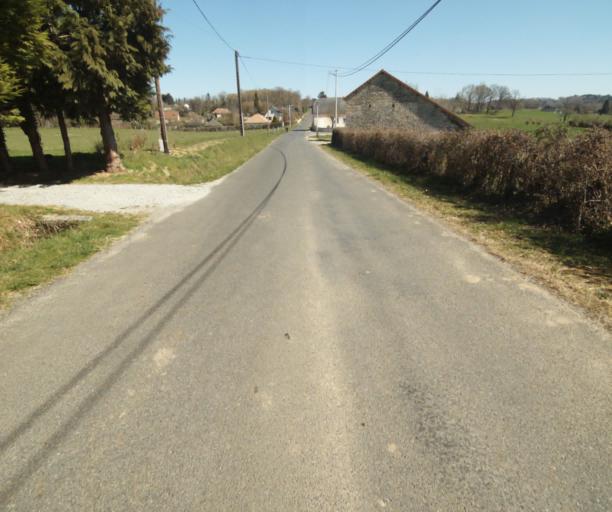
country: FR
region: Limousin
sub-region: Departement de la Correze
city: Saint-Mexant
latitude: 45.3109
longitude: 1.6410
